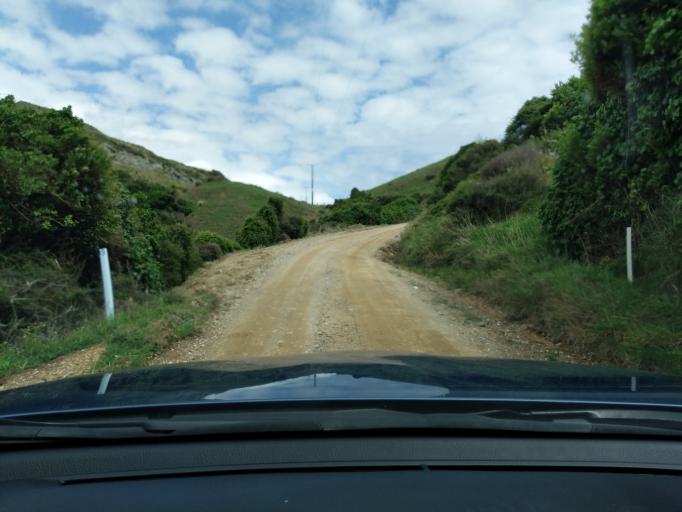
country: NZ
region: Tasman
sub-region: Tasman District
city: Takaka
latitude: -40.6578
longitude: 172.4165
